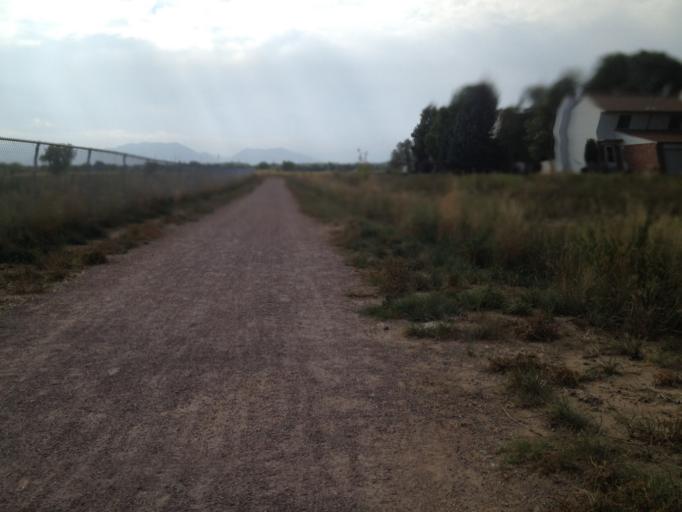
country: US
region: Colorado
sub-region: Boulder County
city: Louisville
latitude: 39.9831
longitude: -105.1155
